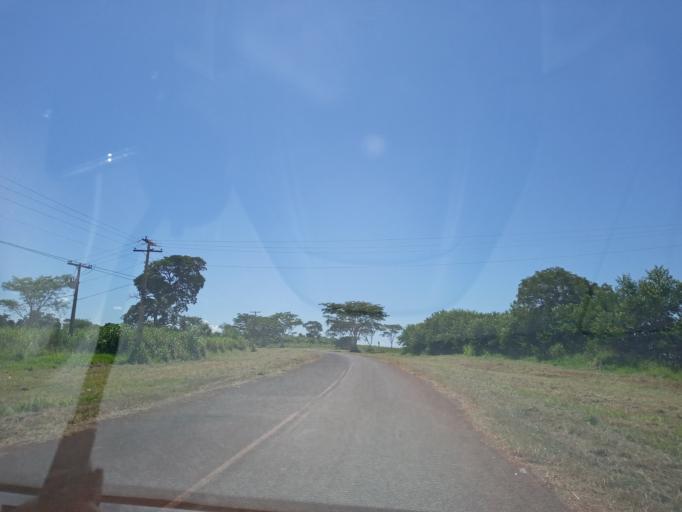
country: BR
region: Goias
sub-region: Itumbiara
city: Itumbiara
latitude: -18.4181
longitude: -49.1360
